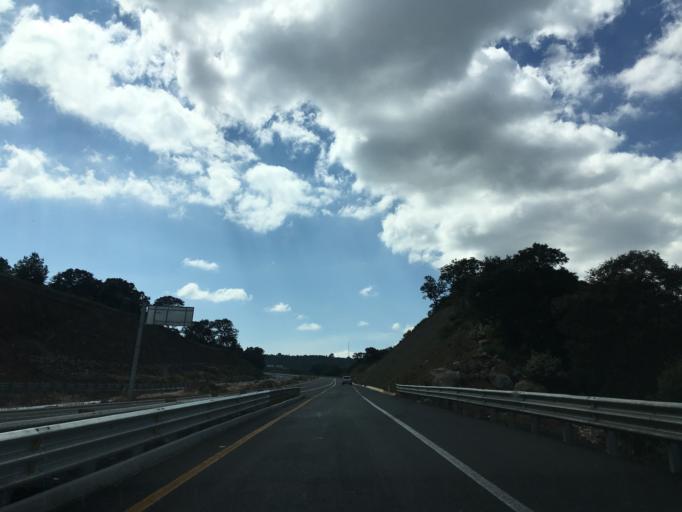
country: MX
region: Michoacan
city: Patzcuaro
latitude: 19.5263
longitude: -101.5676
